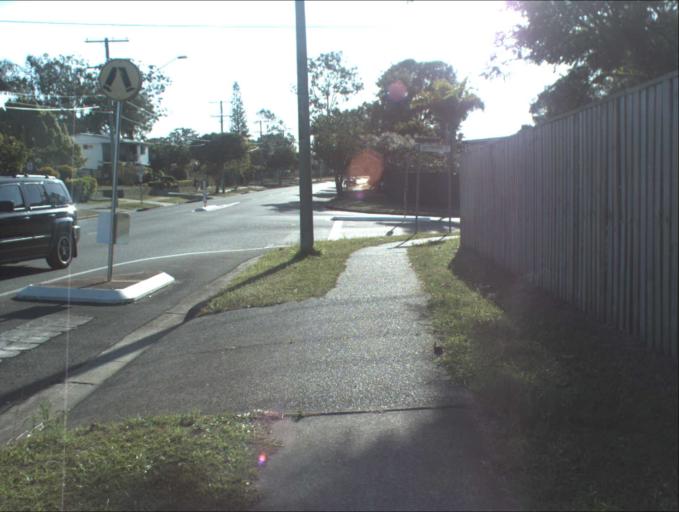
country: AU
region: Queensland
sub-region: Logan
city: Logan City
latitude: -27.6569
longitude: 153.0988
